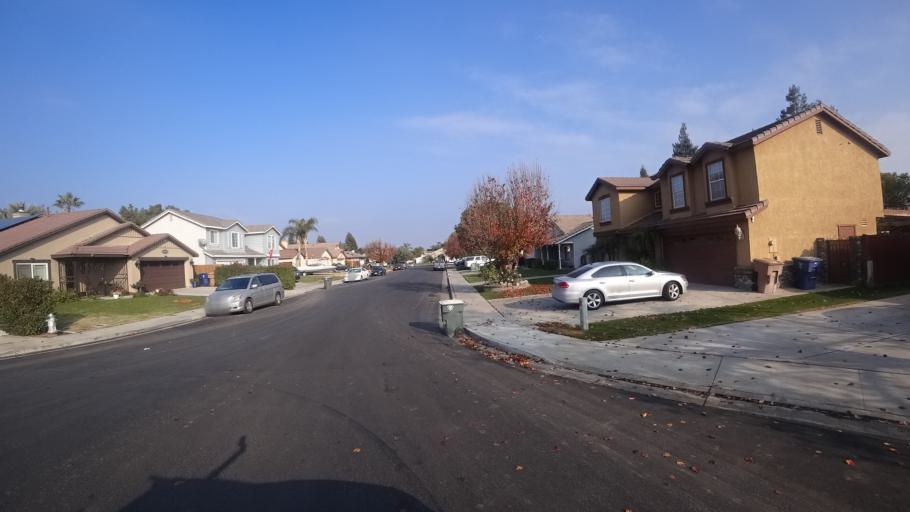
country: US
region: California
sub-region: Kern County
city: Greenfield
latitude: 35.2968
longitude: -119.0685
